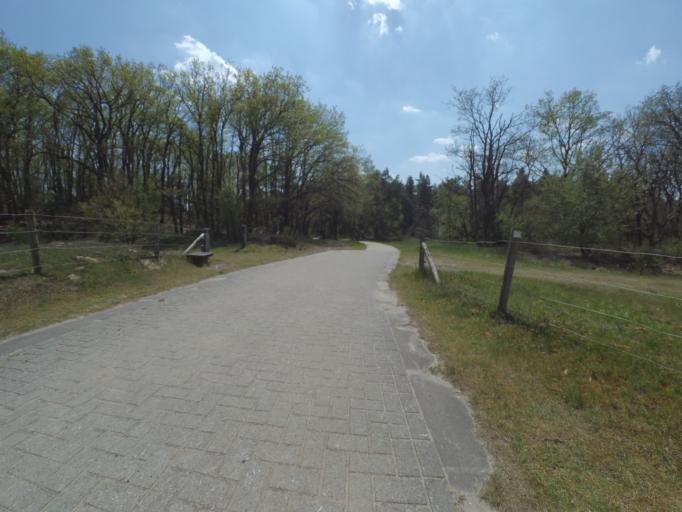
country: NL
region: Gelderland
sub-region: Gemeente Barneveld
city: Garderen
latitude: 52.1946
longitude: 5.7596
